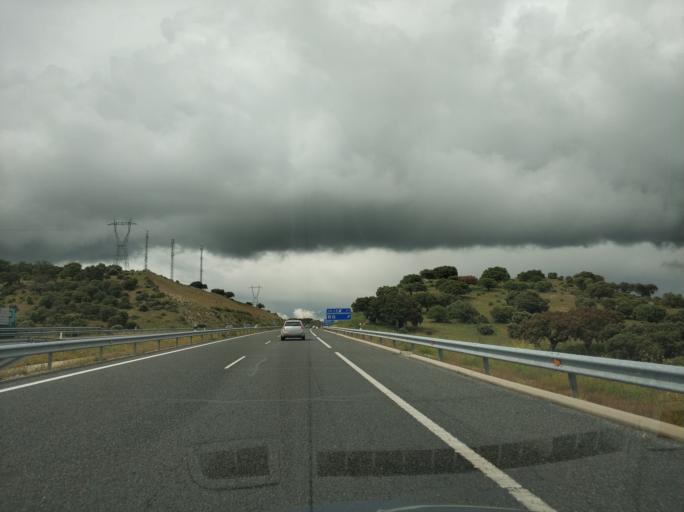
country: ES
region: Castille and Leon
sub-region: Provincia de Salamanca
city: Belena
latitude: 40.6917
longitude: -5.6247
